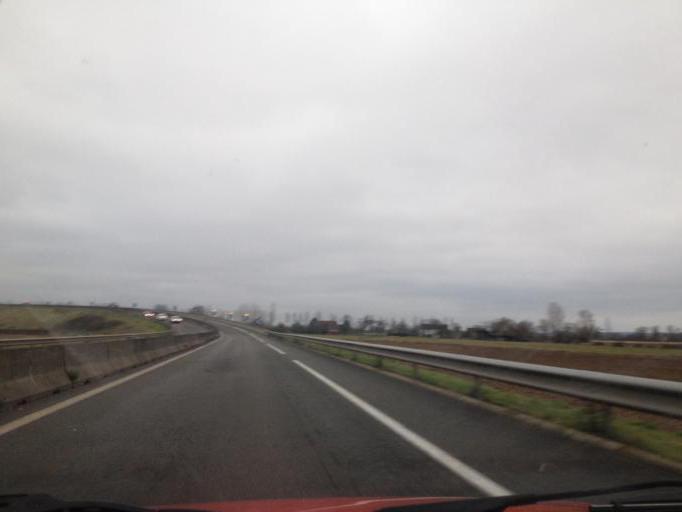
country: FR
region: Auvergne
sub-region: Departement de l'Allier
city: Toulon-sur-Allier
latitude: 46.5047
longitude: 3.3568
